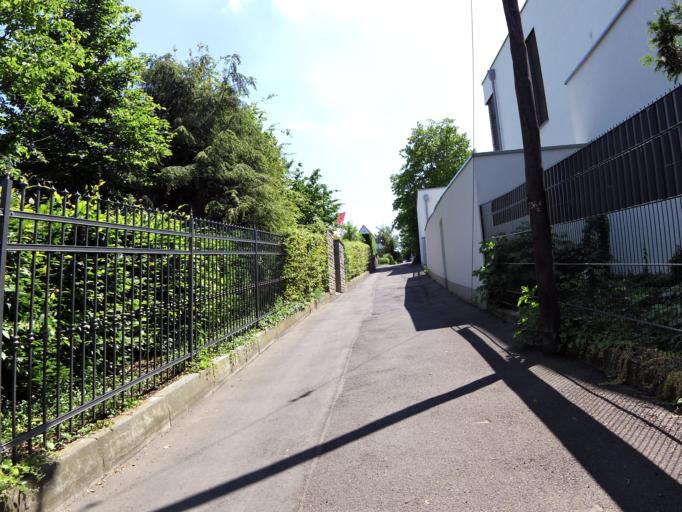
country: DE
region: Bavaria
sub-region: Regierungsbezirk Unterfranken
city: Wuerzburg
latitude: 49.7803
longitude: 9.9509
